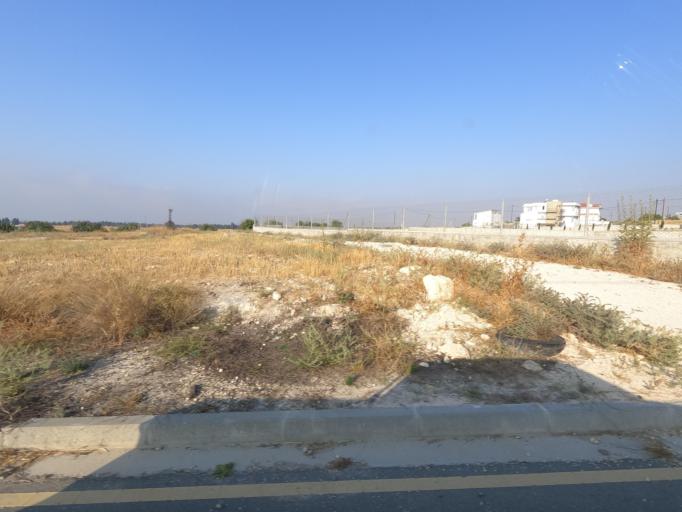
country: CY
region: Larnaka
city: Tersefanou
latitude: 34.8365
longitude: 33.5149
